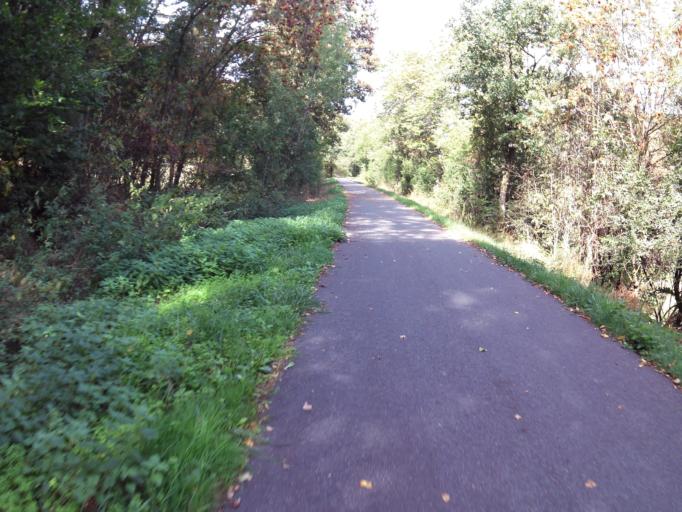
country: DE
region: Rheinland-Pfalz
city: Kickeshausen
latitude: 50.0594
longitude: 6.2481
